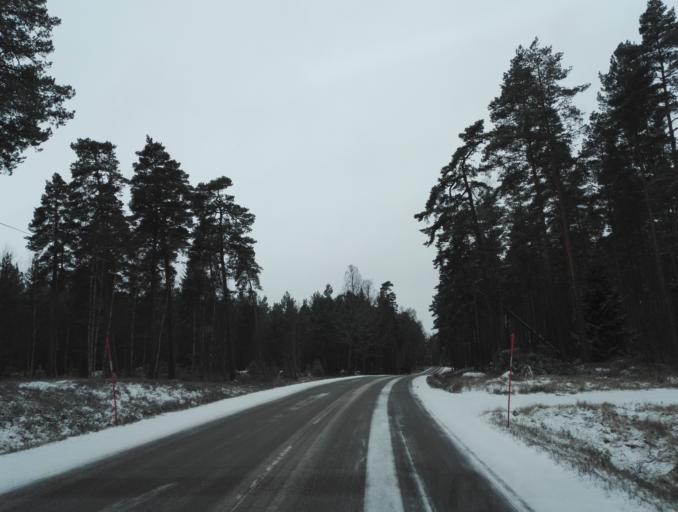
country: SE
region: Kronoberg
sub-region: Lessebo Kommun
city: Hovmantorp
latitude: 56.6618
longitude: 15.1458
